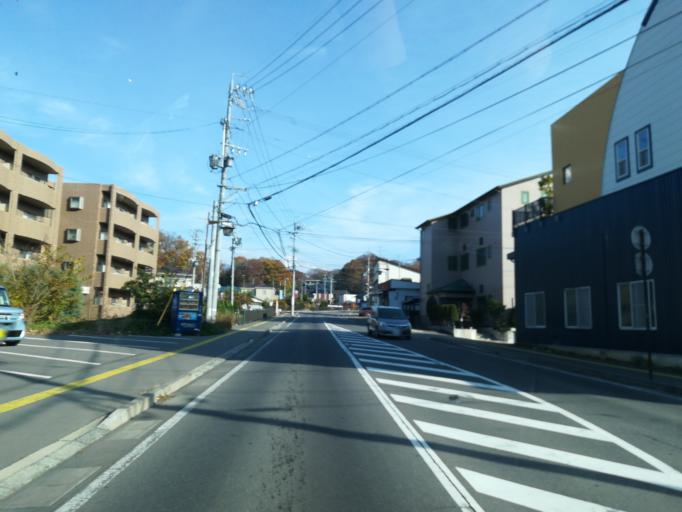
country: JP
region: Nagano
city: Ueda
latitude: 36.3942
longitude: 138.2667
